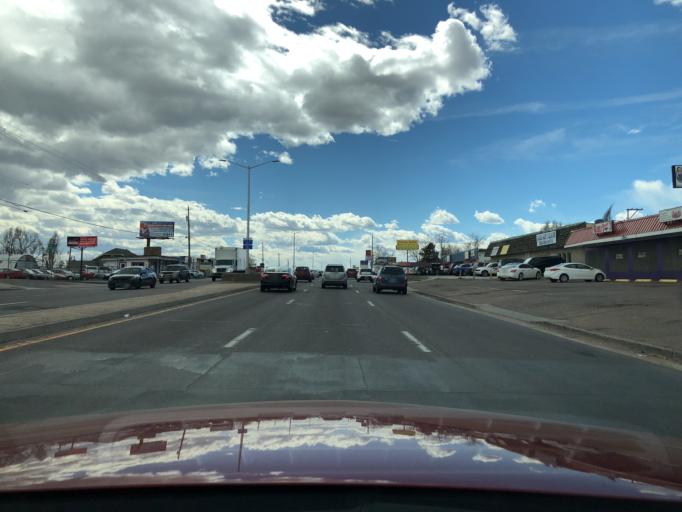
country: US
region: Colorado
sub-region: Adams County
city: Berkley
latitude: 39.8178
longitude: -105.0253
